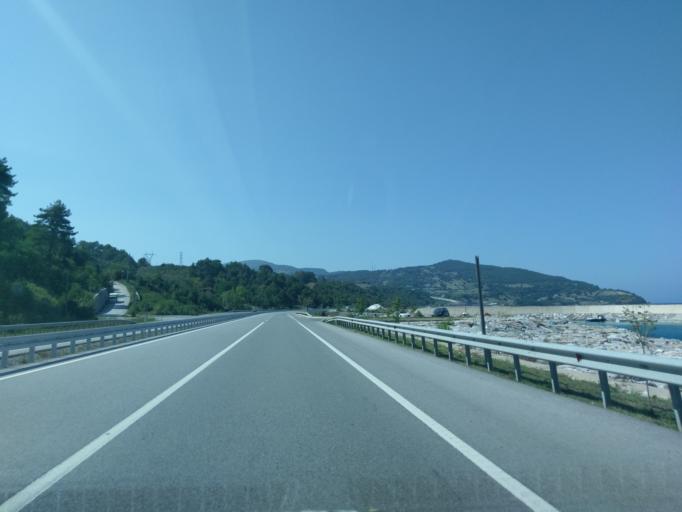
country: TR
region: Sinop
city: Dikmen
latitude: 41.7147
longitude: 35.2791
